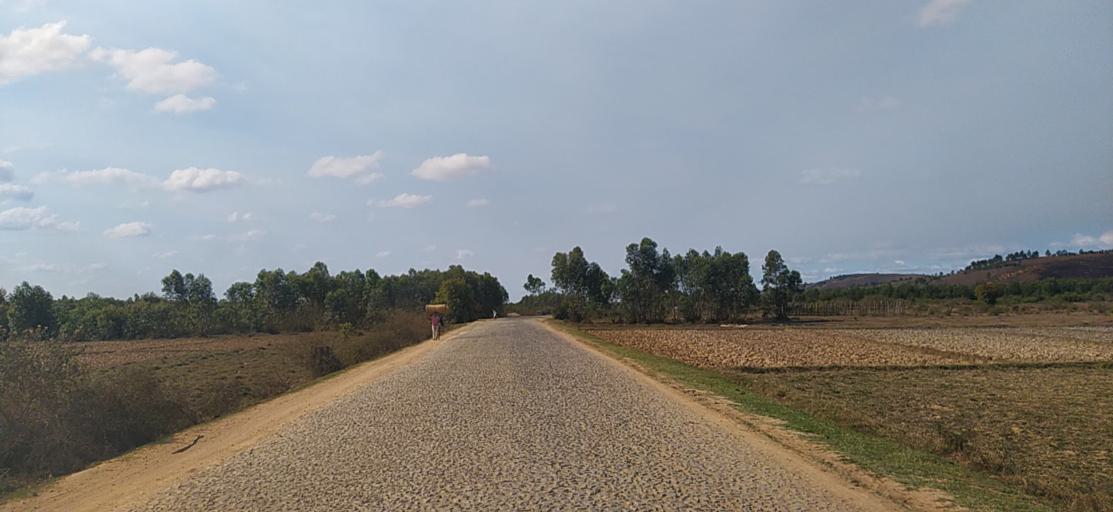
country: MG
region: Alaotra Mangoro
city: Moramanga
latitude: -18.6892
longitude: 48.2711
